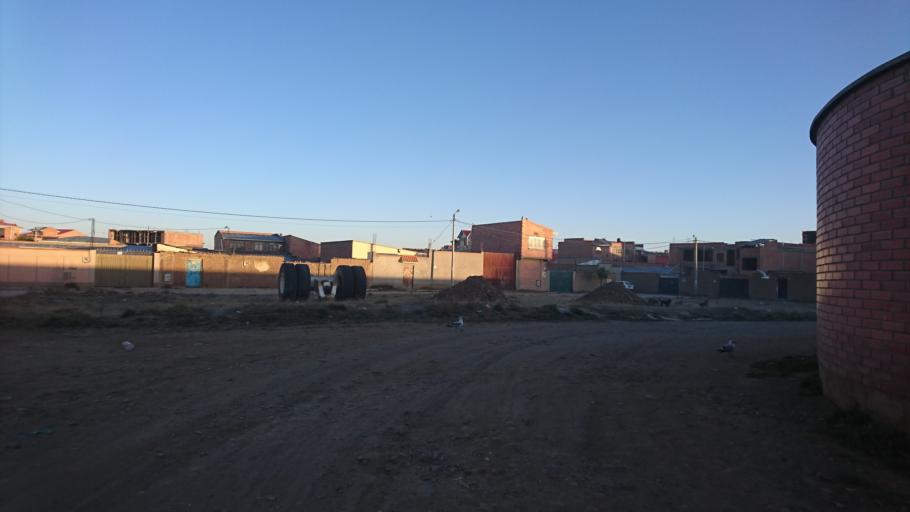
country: BO
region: La Paz
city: La Paz
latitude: -16.5003
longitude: -68.1881
